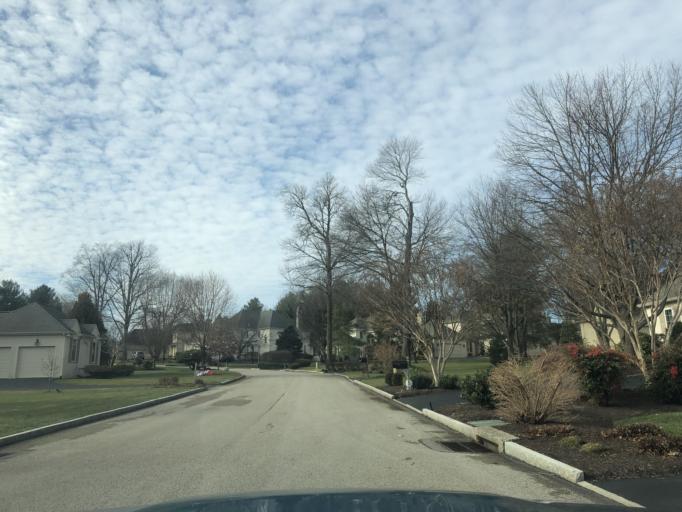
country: US
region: Pennsylvania
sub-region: Delaware County
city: Radnor
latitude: 40.0320
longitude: -75.3466
